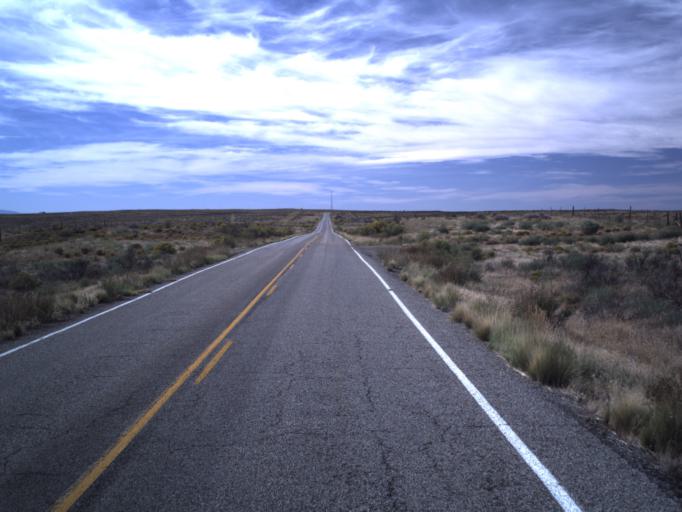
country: US
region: Utah
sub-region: San Juan County
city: Blanding
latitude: 37.3515
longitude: -109.3471
